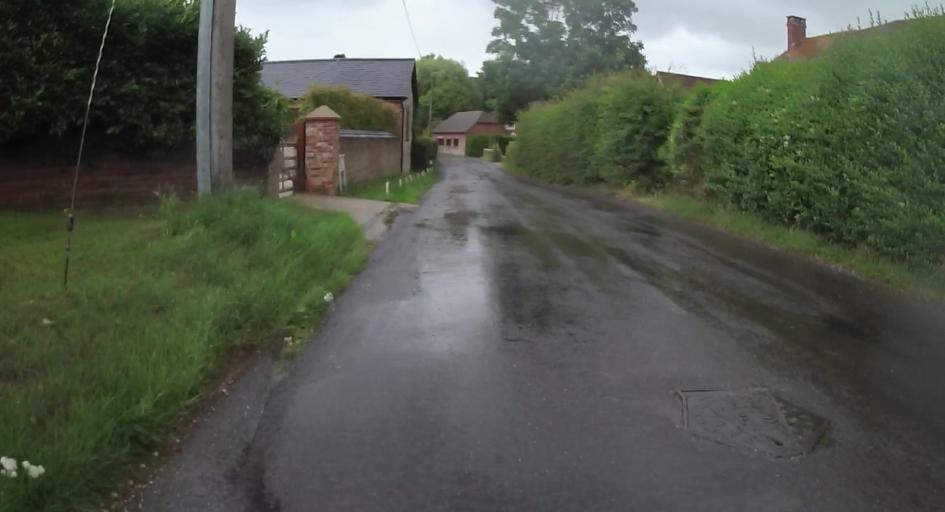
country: GB
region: England
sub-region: Hampshire
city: Long Sutton
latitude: 51.1827
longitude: -0.9182
